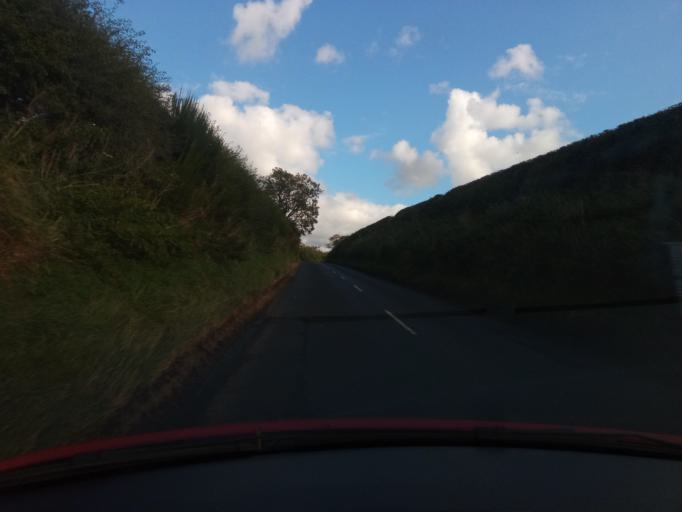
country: GB
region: Scotland
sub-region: The Scottish Borders
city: Kelso
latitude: 55.5712
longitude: -2.3739
